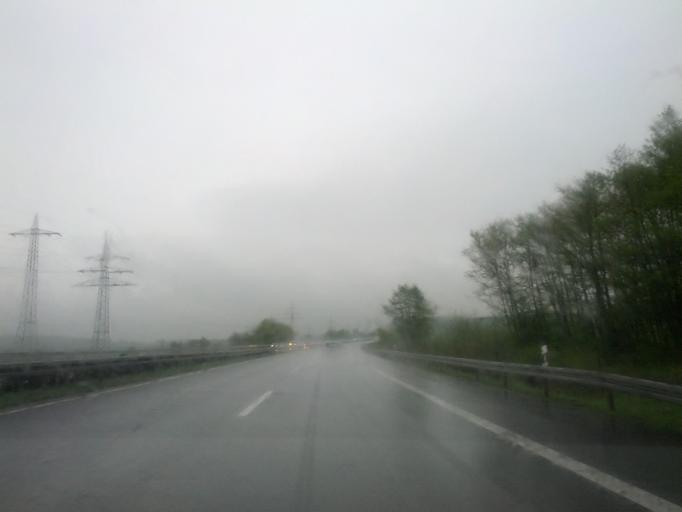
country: DE
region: Hesse
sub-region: Regierungsbezirk Giessen
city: Alten Buseck
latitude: 50.6347
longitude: 8.7355
